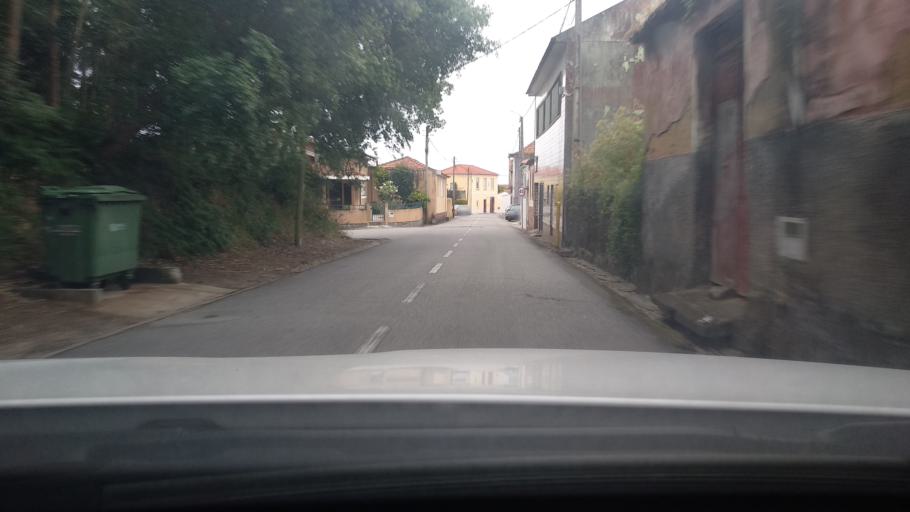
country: PT
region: Aveiro
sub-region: Espinho
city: Souto
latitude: 40.9814
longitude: -8.6254
